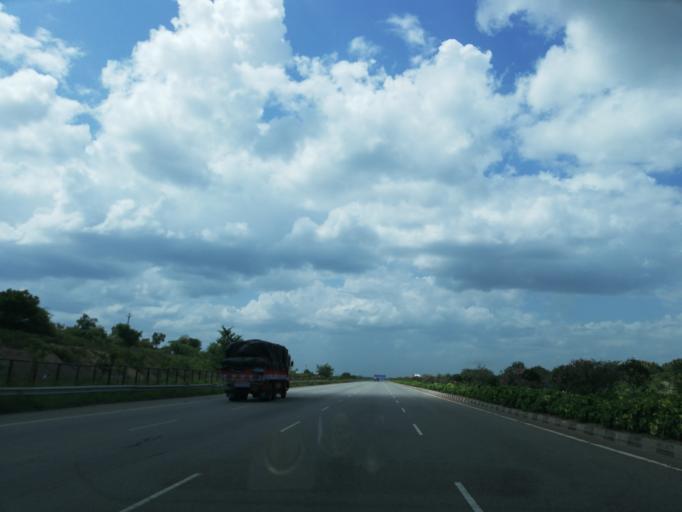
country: IN
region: Telangana
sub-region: Medak
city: Serilingampalle
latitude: 17.4346
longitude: 78.2614
